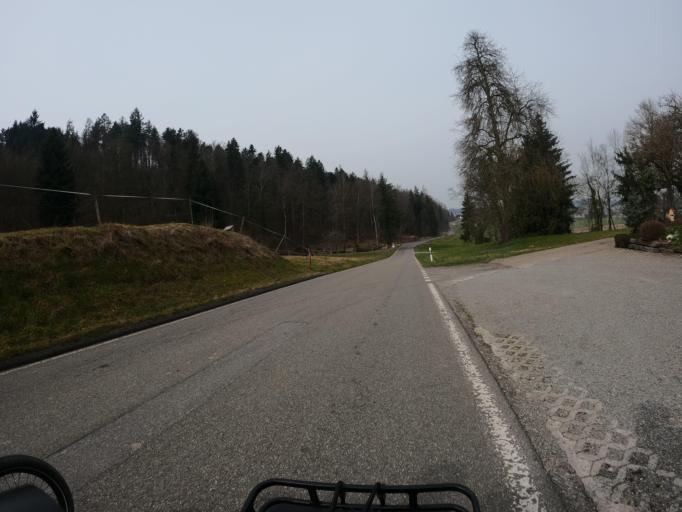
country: CH
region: Aargau
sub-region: Bezirk Baden
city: Mellingen
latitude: 47.4059
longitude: 8.2712
